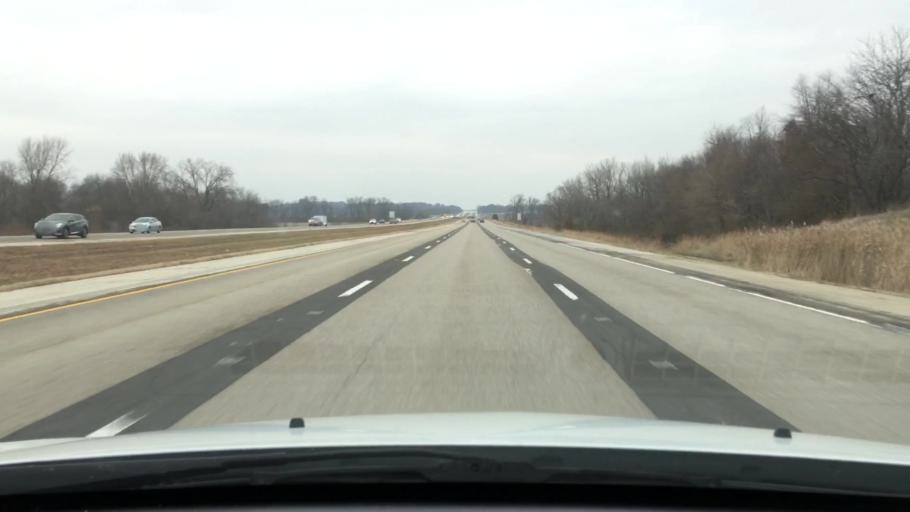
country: US
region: Illinois
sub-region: Logan County
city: Lincoln
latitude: 40.1196
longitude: -89.4164
